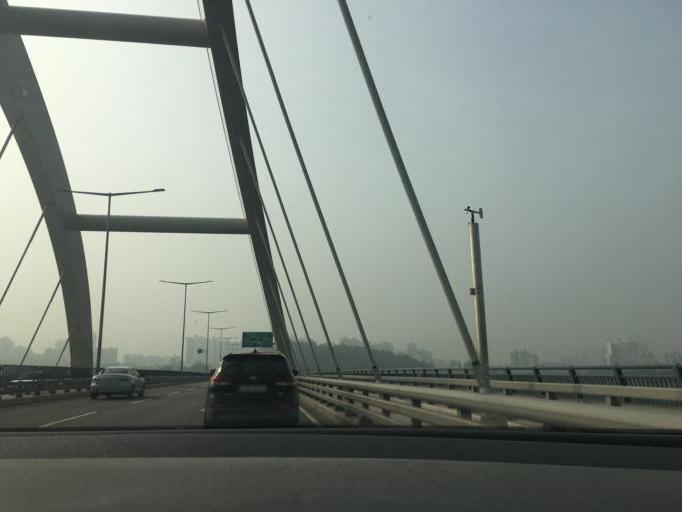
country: KR
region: Gyeonggi-do
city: Guri-si
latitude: 37.5682
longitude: 127.1324
